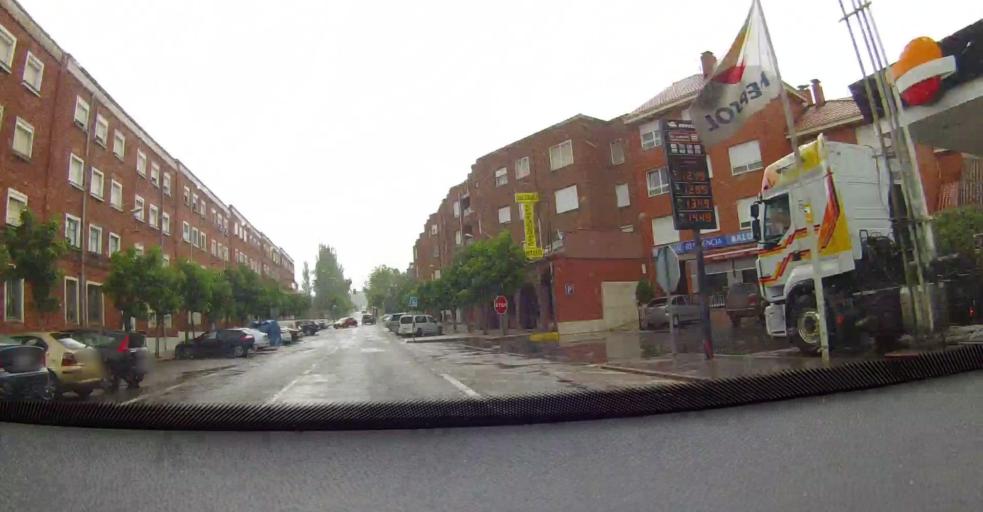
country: ES
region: Castille and Leon
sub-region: Provincia de Palencia
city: Saldana
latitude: 42.5185
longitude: -4.7363
